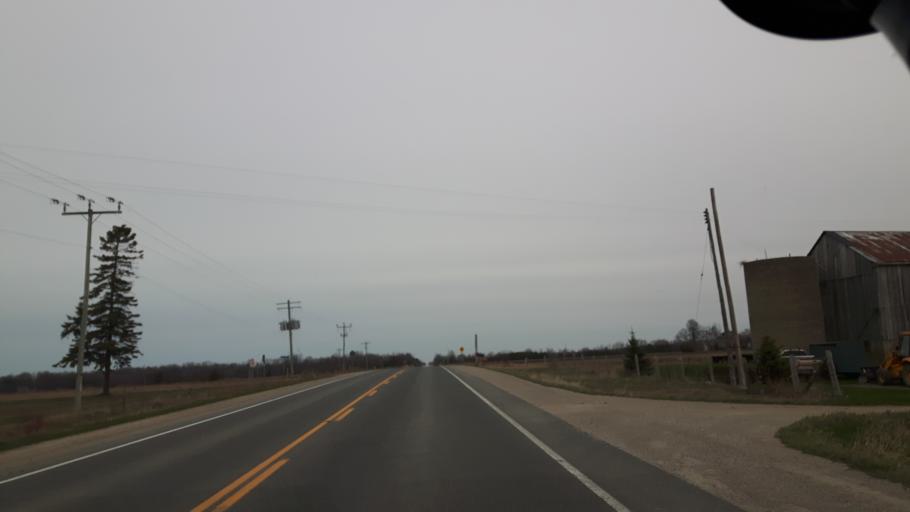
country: CA
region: Ontario
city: Goderich
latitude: 43.6069
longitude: -81.7056
